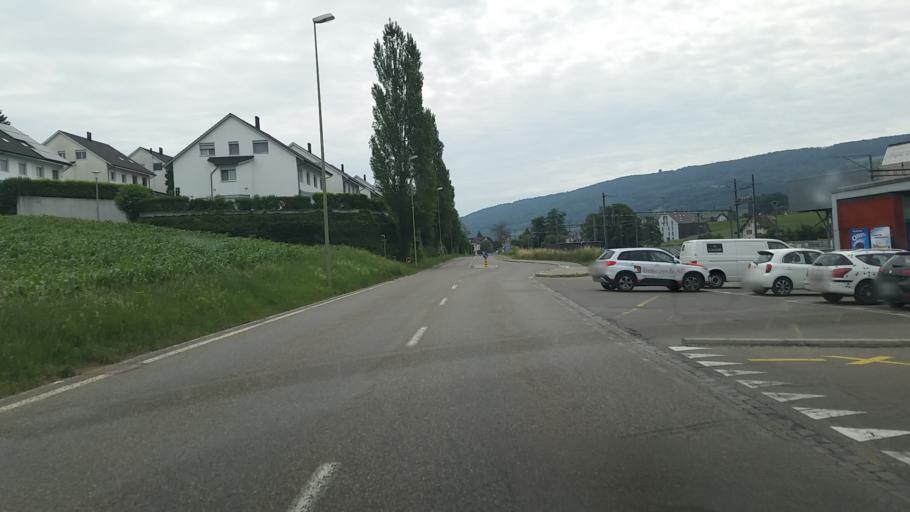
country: CH
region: Aargau
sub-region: Bezirk Baden
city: Unterehrendingen
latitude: 47.5115
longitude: 8.3695
